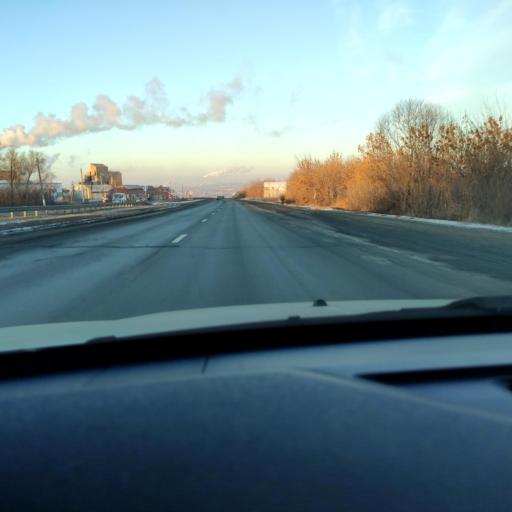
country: RU
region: Samara
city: Smyshlyayevka
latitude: 53.2591
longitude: 50.4446
